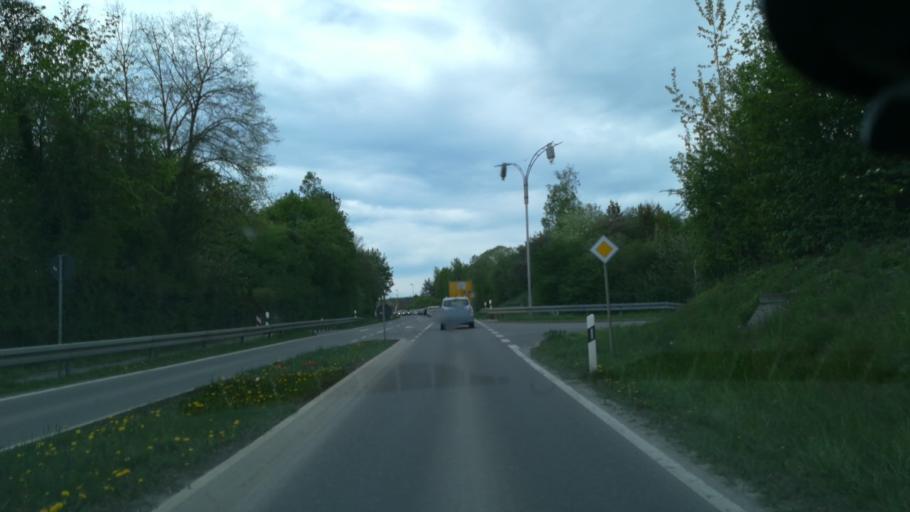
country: DE
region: Baden-Wuerttemberg
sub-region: Freiburg Region
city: Radolfzell am Bodensee
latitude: 47.7486
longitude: 8.9795
